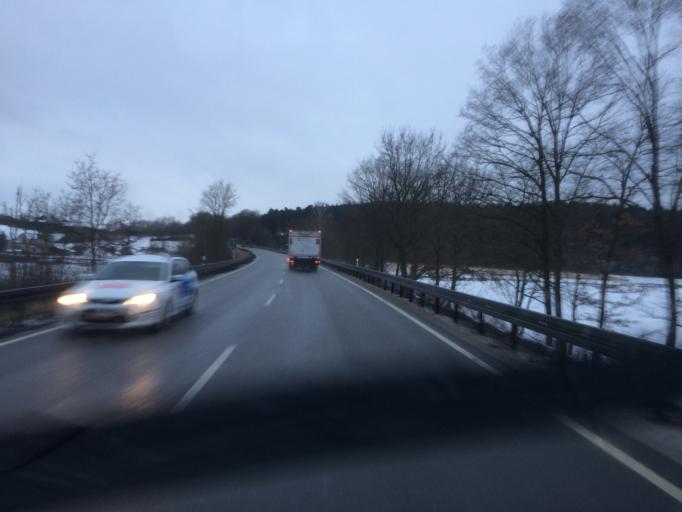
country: DE
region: Bavaria
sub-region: Upper Palatinate
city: Schwandorf in Bayern
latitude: 49.3478
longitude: 12.1004
